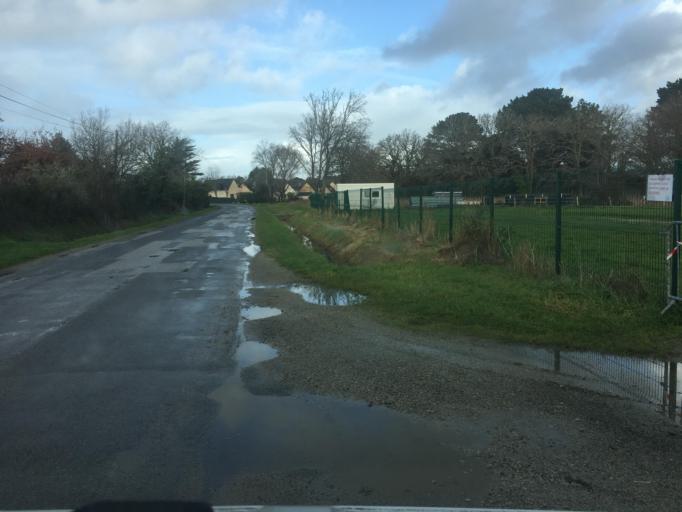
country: FR
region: Brittany
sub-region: Departement du Morbihan
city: Sarzeau
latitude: 47.4998
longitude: -2.7669
